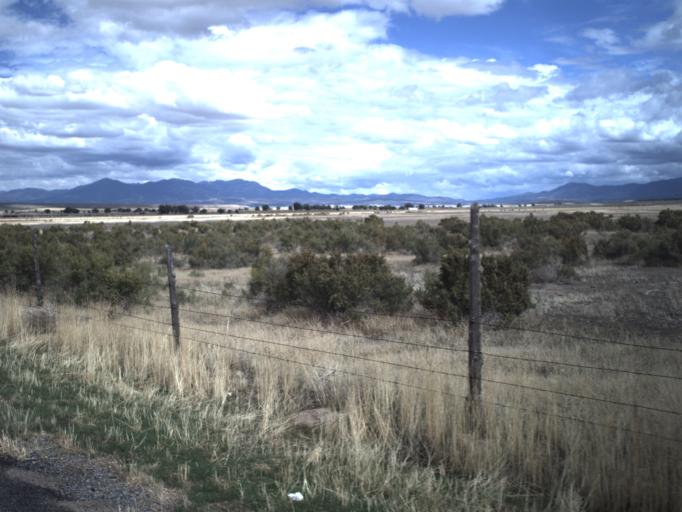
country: US
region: Utah
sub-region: Millard County
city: Fillmore
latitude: 39.0193
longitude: -112.4100
